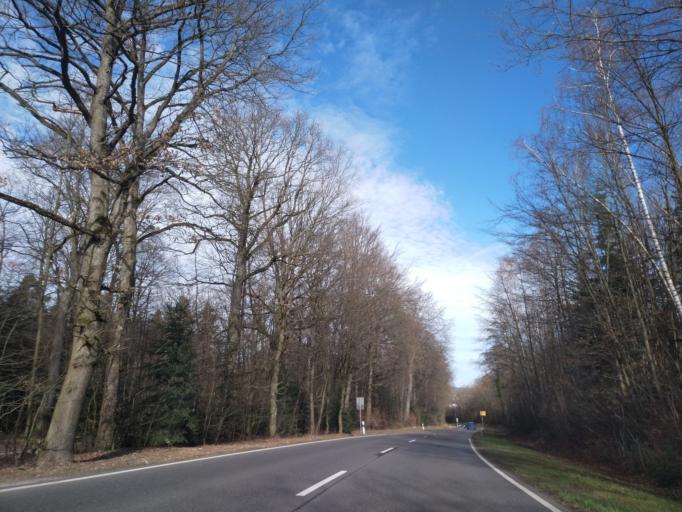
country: DE
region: Baden-Wuerttemberg
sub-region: Karlsruhe Region
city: Birkenfeld
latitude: 48.8674
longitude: 8.6617
